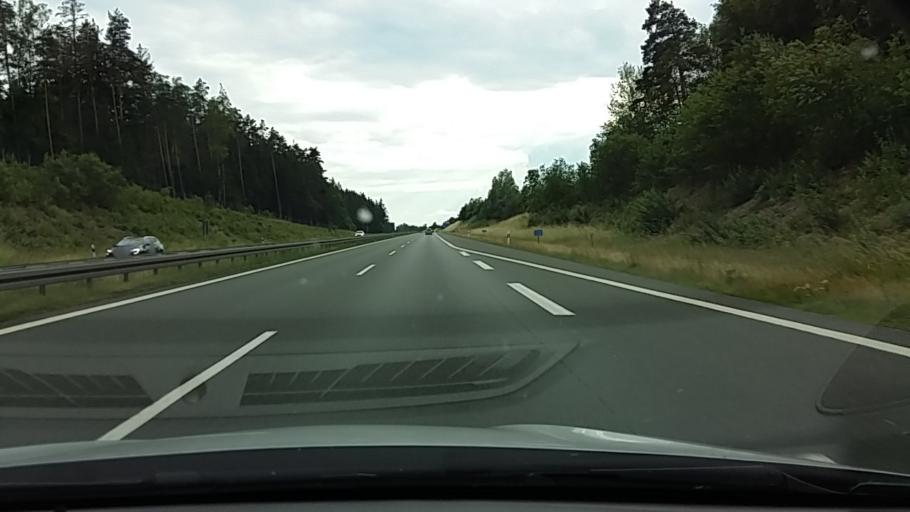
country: DE
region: Bavaria
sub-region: Upper Palatinate
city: Leuchtenberg
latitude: 49.5746
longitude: 12.2684
